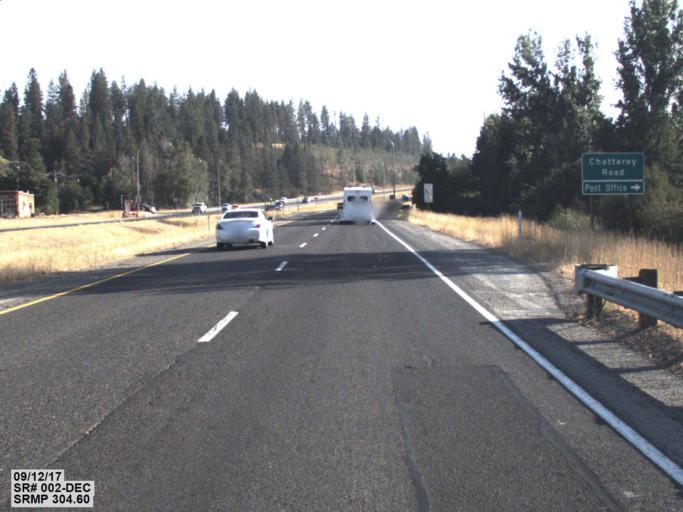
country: US
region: Washington
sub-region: Spokane County
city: Mead
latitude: 47.8909
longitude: -117.3537
